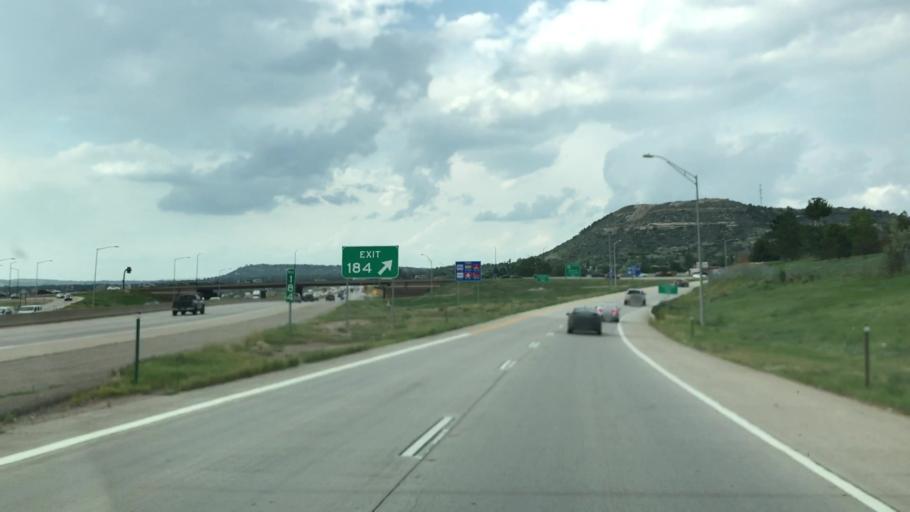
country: US
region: Colorado
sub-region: Douglas County
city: Castle Rock
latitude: 39.4102
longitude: -104.8660
